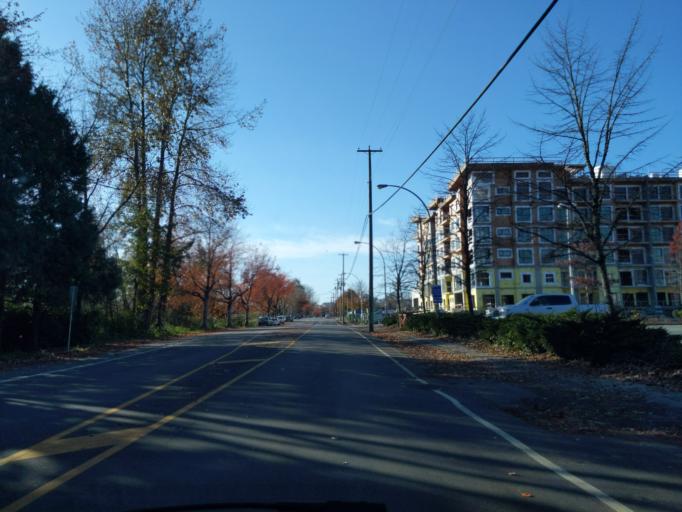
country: CA
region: British Columbia
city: New Westminster
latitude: 49.2027
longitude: -122.8699
